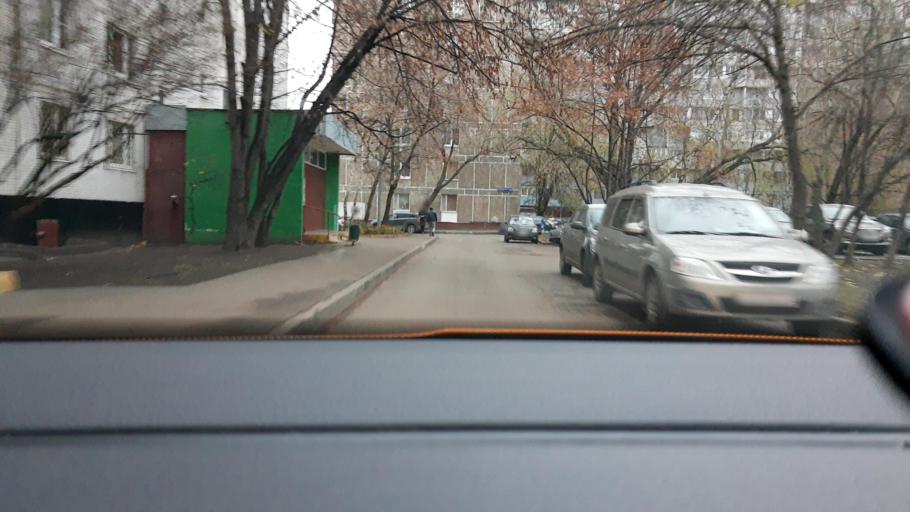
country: RU
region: Moscow
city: Bibirevo
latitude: 55.8971
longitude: 37.6259
